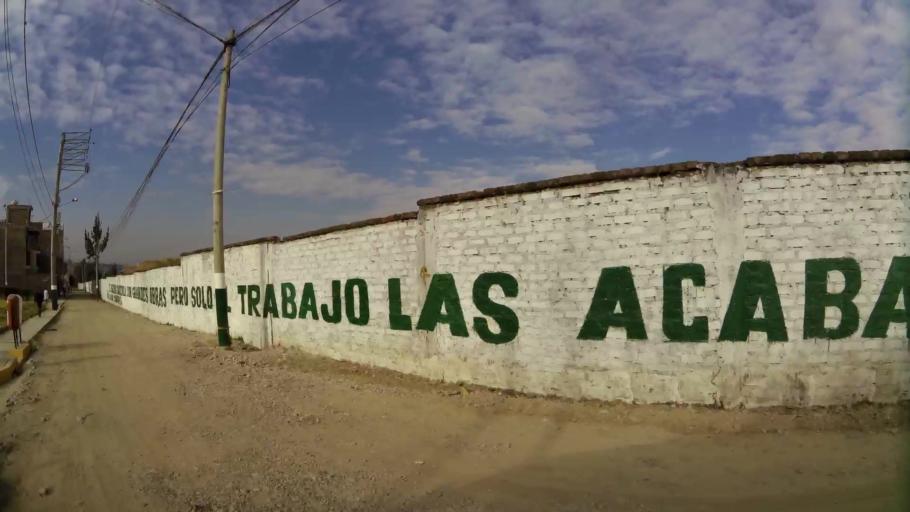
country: PE
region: Junin
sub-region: Provincia de Huancayo
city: Huancayo
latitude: -12.0440
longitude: -75.1920
